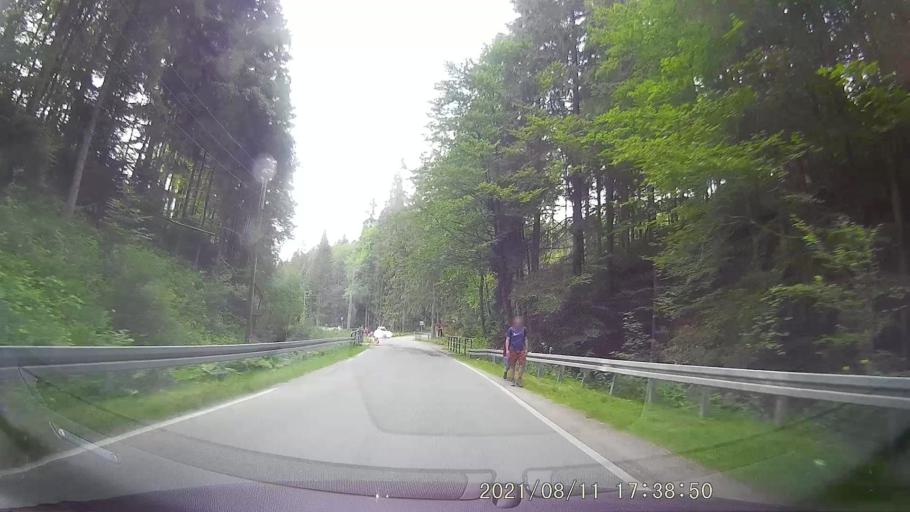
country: PL
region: Lower Silesian Voivodeship
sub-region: Powiat klodzki
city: Duszniki-Zdroj
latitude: 50.3463
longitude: 16.4001
